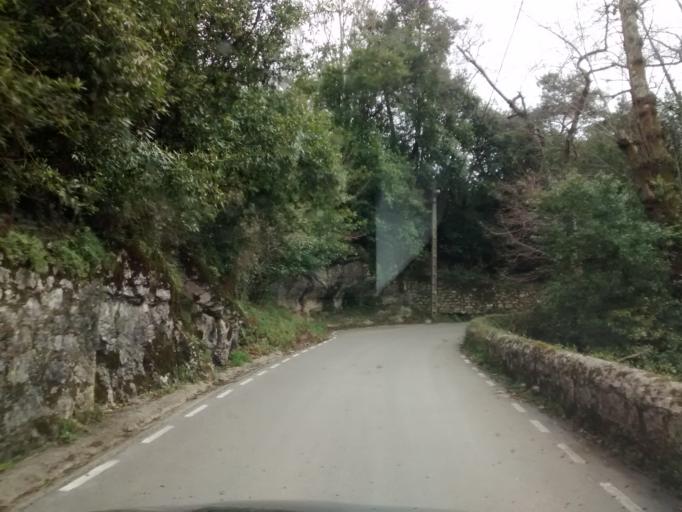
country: ES
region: Cantabria
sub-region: Provincia de Cantabria
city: Entrambasaguas
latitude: 43.3504
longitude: -3.7055
